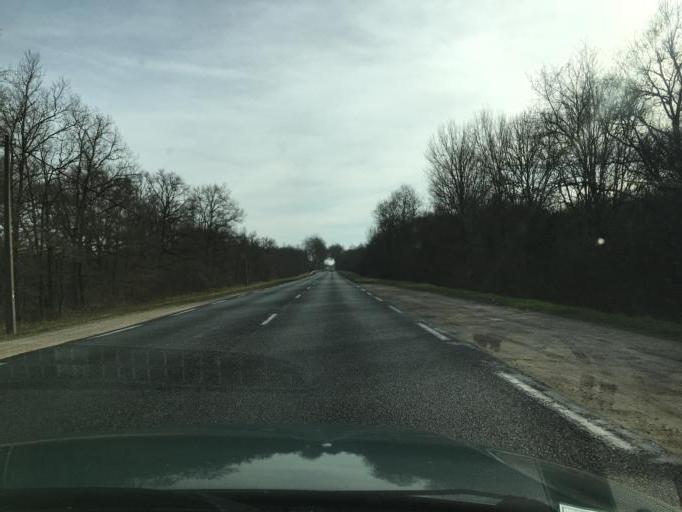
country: FR
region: Centre
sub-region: Departement du Loiret
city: Saint-Cyr-en-Val
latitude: 47.7814
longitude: 1.9351
